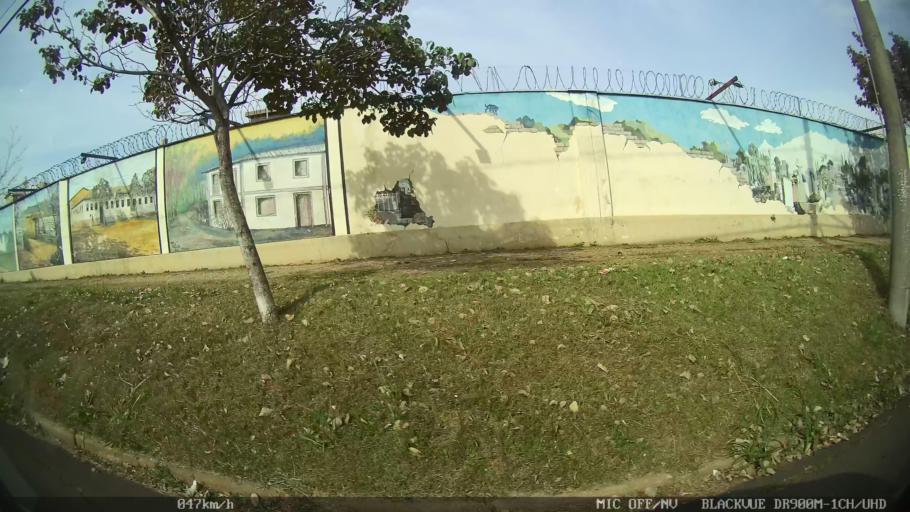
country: BR
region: Sao Paulo
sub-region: Piracicaba
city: Piracicaba
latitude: -22.7291
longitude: -47.6358
